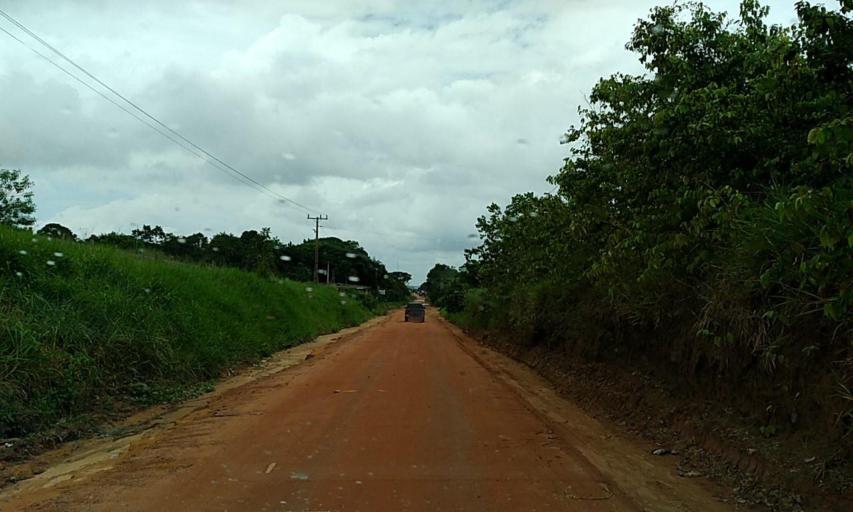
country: BR
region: Para
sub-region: Senador Jose Porfirio
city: Senador Jose Porfirio
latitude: -2.5832
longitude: -51.9374
